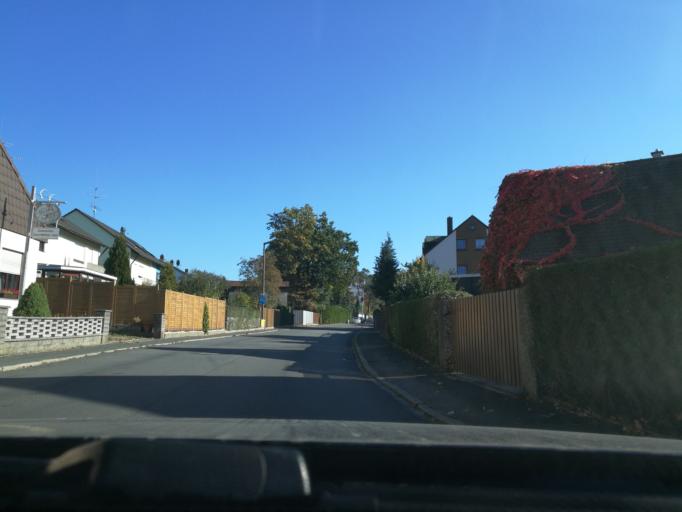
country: DE
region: Bavaria
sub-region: Regierungsbezirk Mittelfranken
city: Zirndorf
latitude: 49.4592
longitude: 10.9292
